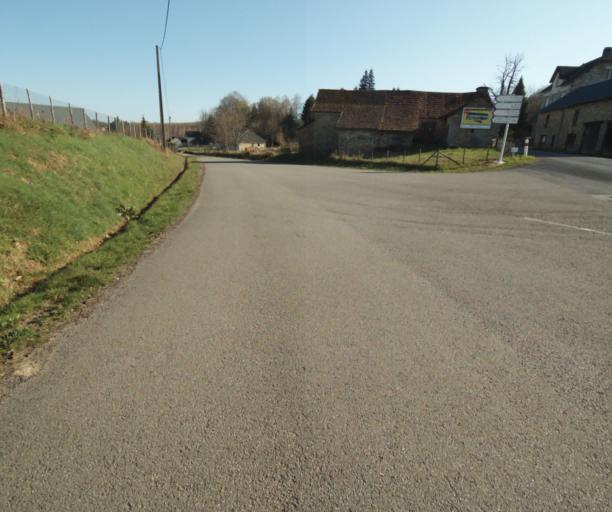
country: FR
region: Limousin
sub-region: Departement de la Correze
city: Saint-Clement
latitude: 45.3154
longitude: 1.6792
